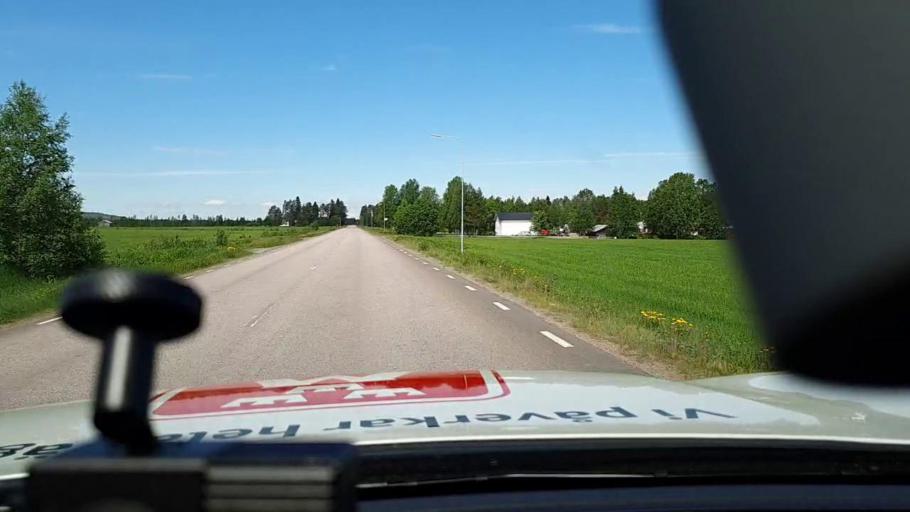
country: SE
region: Norrbotten
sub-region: Lulea Kommun
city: Sodra Sunderbyn
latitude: 65.6380
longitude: 21.9096
